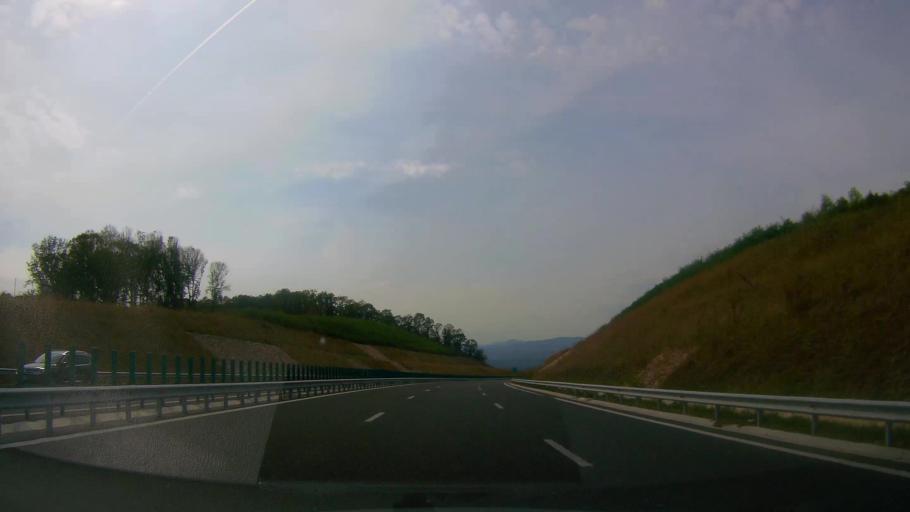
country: RO
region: Cluj
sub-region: Comuna Floresti
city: Luna de Sus
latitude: 46.7833
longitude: 23.4159
